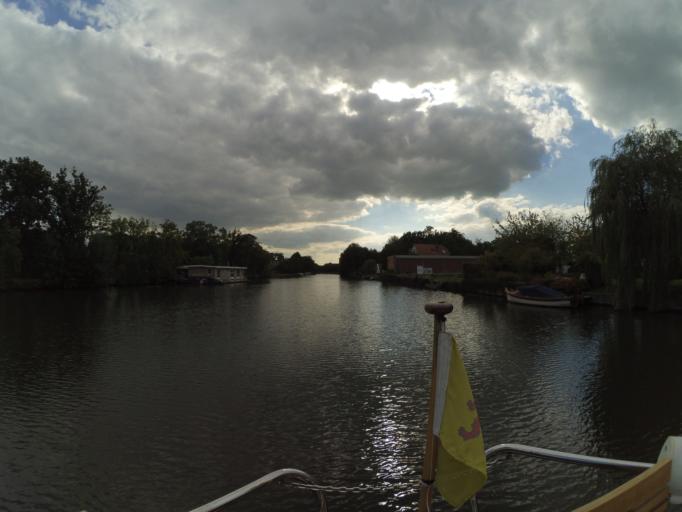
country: NL
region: Utrecht
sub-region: Stichtse Vecht
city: Maarssen
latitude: 52.1495
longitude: 5.0342
